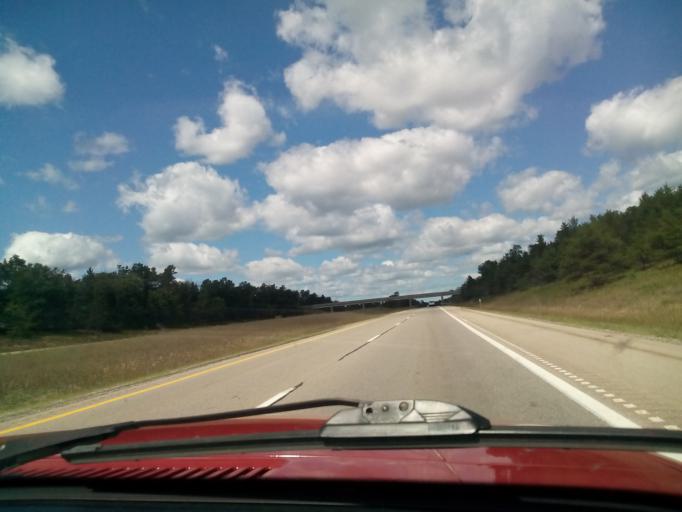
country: US
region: Michigan
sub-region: Crawford County
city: Grayling
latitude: 44.6678
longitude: -84.6963
